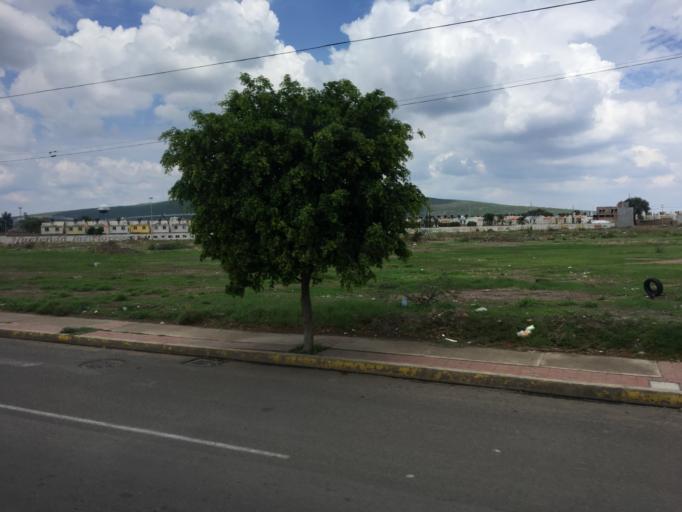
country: MX
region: Guanajuato
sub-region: Irapuato
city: Ex-Hacienda del Copal
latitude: 20.7115
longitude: -101.3514
